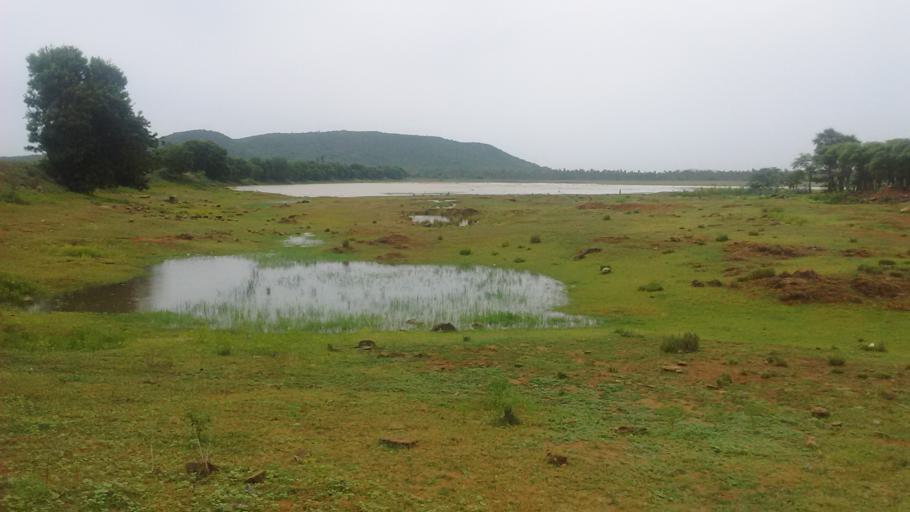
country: IN
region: Tamil Nadu
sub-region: Kancheepuram
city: Madambakkam
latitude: 12.9105
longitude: 79.9963
